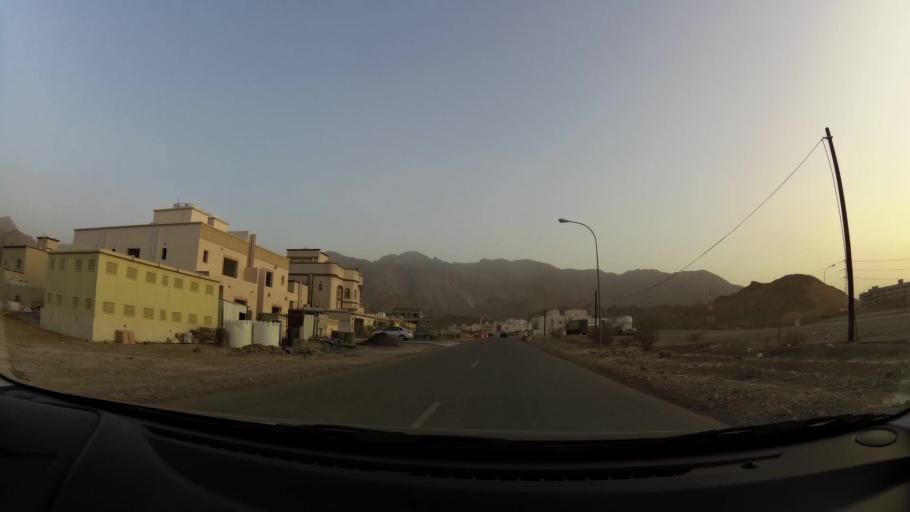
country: OM
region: Muhafazat Masqat
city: Bawshar
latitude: 23.4796
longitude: 58.3078
